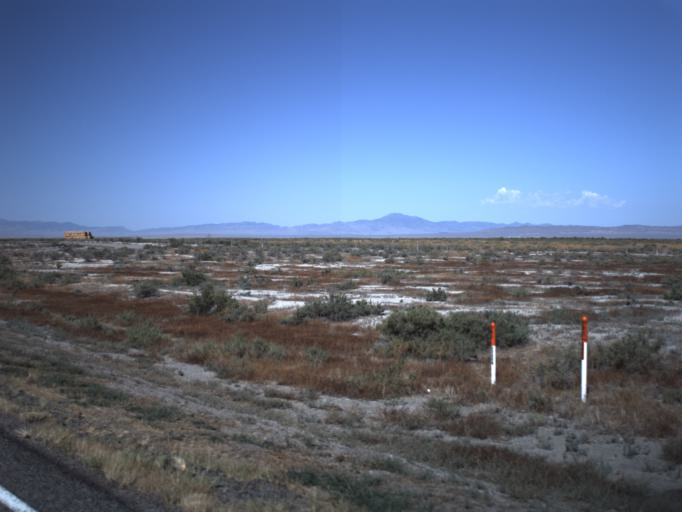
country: US
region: Utah
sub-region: Millard County
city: Delta
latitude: 39.3281
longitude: -112.7259
